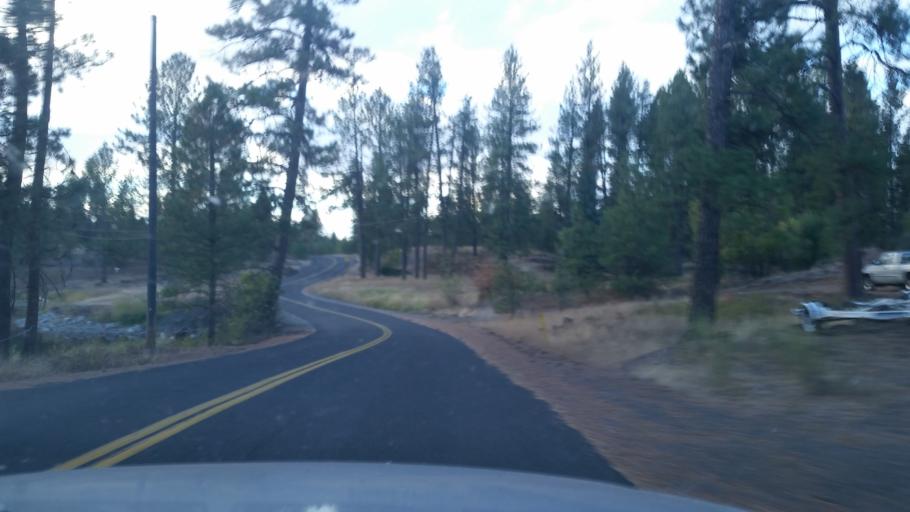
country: US
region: Washington
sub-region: Spokane County
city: Medical Lake
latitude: 47.5415
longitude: -117.6881
